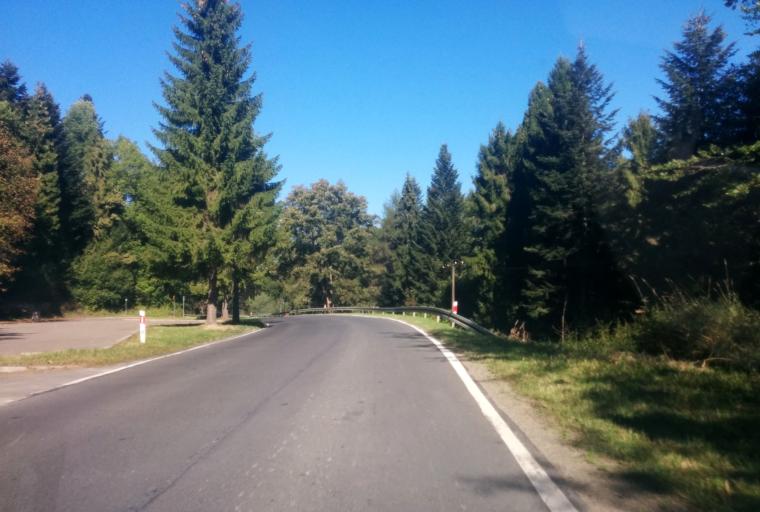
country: PL
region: Subcarpathian Voivodeship
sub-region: Powiat bieszczadzki
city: Lutowiska
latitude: 49.2848
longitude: 22.6822
